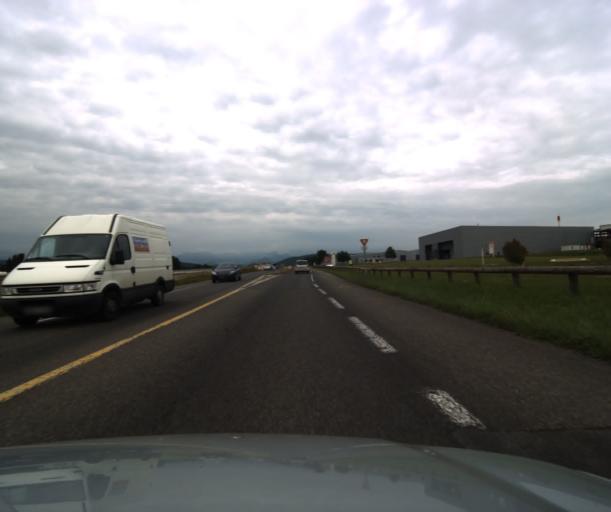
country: FR
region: Midi-Pyrenees
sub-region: Departement des Hautes-Pyrenees
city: Ossun
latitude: 43.1733
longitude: 0.0006
